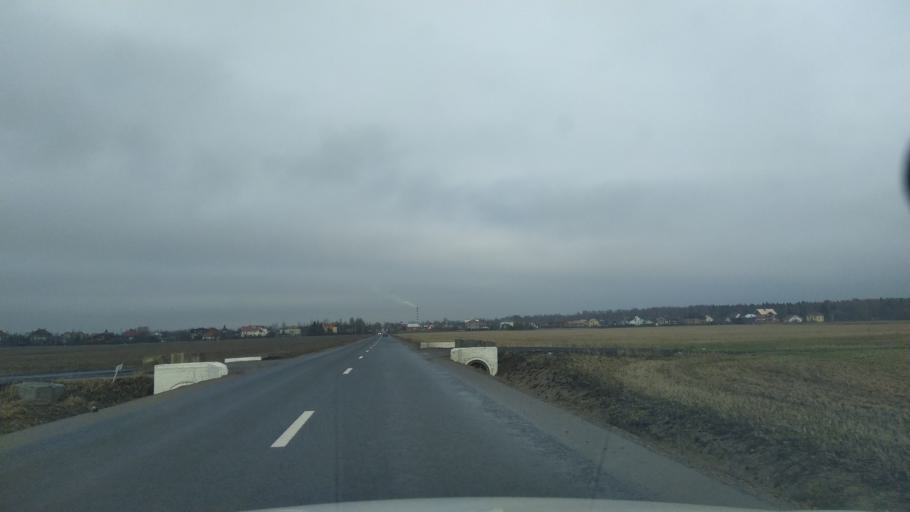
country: RU
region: St.-Petersburg
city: Aleksandrovskaya
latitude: 59.7182
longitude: 30.3401
